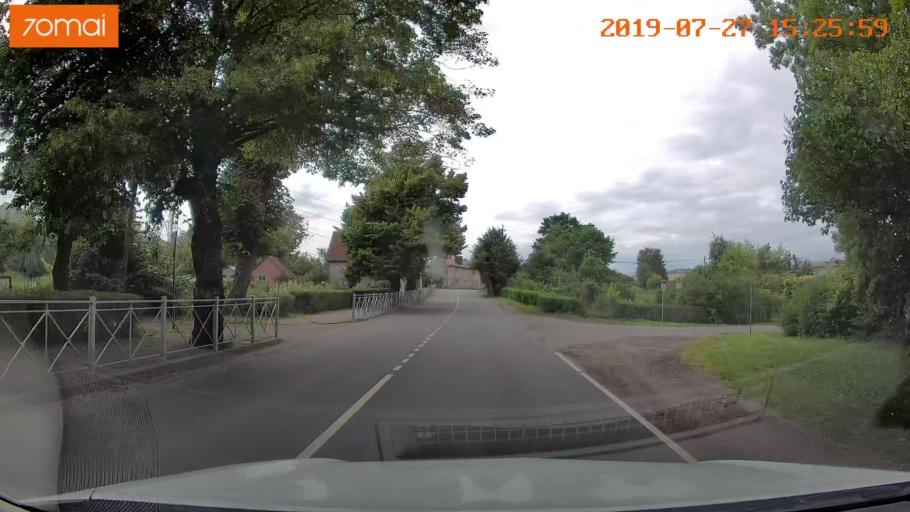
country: RU
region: Kaliningrad
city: Nesterov
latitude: 54.6306
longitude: 22.5790
